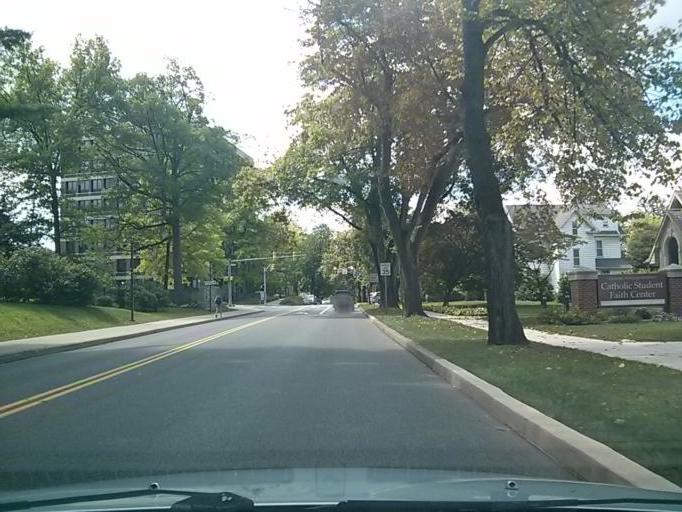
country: US
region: Pennsylvania
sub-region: Centre County
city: State College
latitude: 40.8008
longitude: -77.8691
